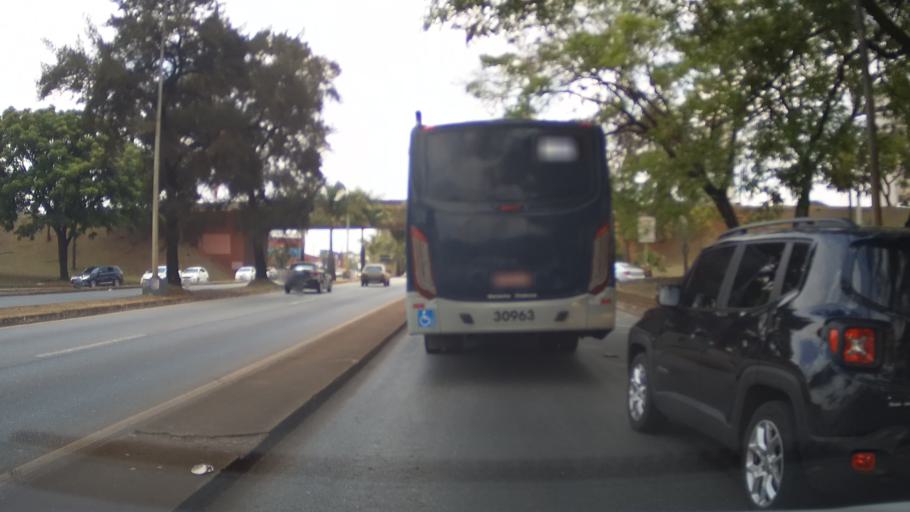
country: BR
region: Minas Gerais
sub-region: Belo Horizonte
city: Belo Horizonte
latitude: -19.9734
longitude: -43.9459
